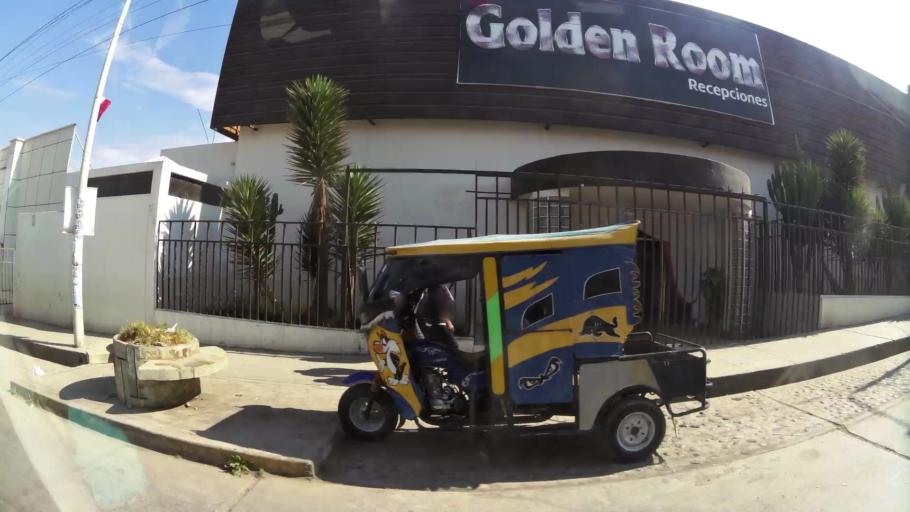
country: PE
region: Junin
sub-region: Provincia de Huancayo
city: El Tambo
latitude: -12.0717
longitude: -75.2179
